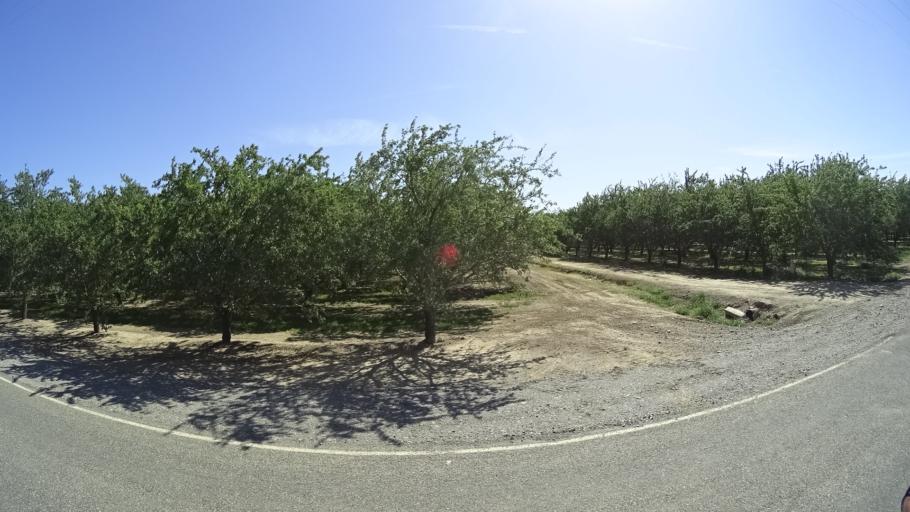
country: US
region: California
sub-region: Glenn County
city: Willows
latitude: 39.6262
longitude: -122.1788
